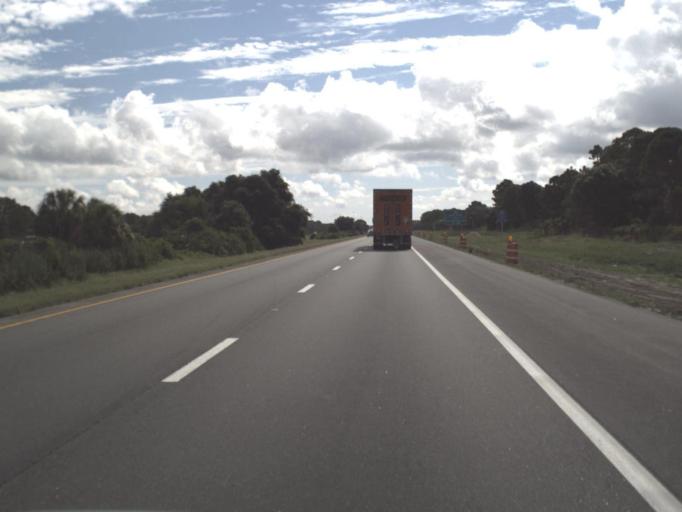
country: US
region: Florida
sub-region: Sarasota County
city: Warm Mineral Springs
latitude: 27.0994
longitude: -82.2259
